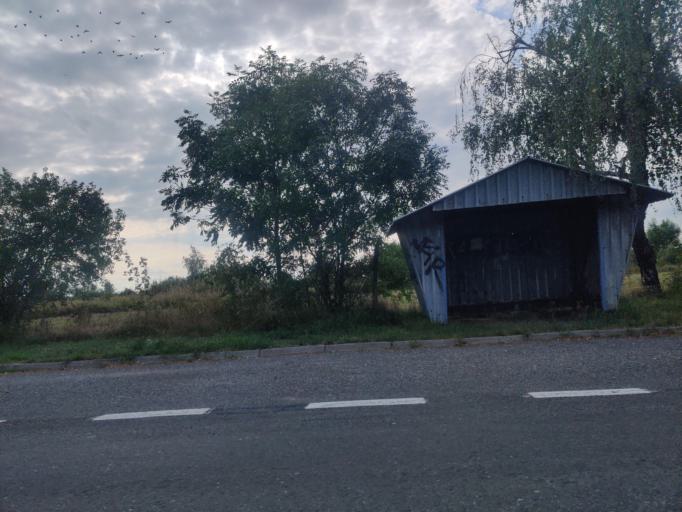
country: PL
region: Greater Poland Voivodeship
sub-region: Konin
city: Konin
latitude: 52.2744
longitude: 18.2668
